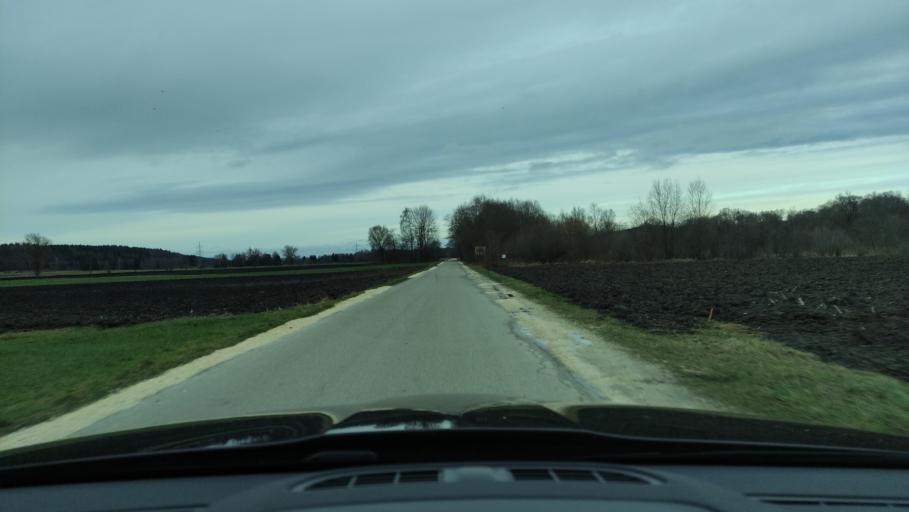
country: DE
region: Bavaria
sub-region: Swabia
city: Breitenthal
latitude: 48.2368
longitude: 10.3102
